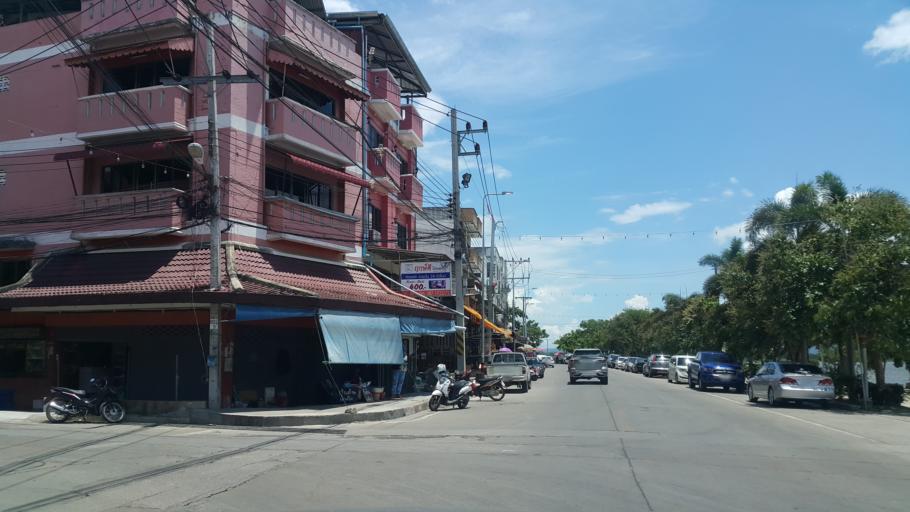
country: TH
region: Phayao
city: Phayao
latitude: 19.1662
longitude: 99.8962
